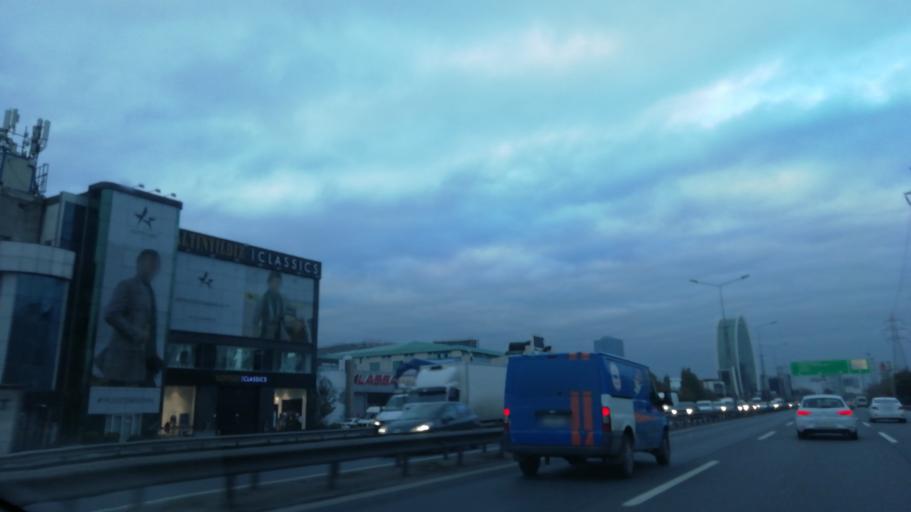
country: TR
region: Istanbul
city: Mahmutbey
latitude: 41.0220
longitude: 28.8121
